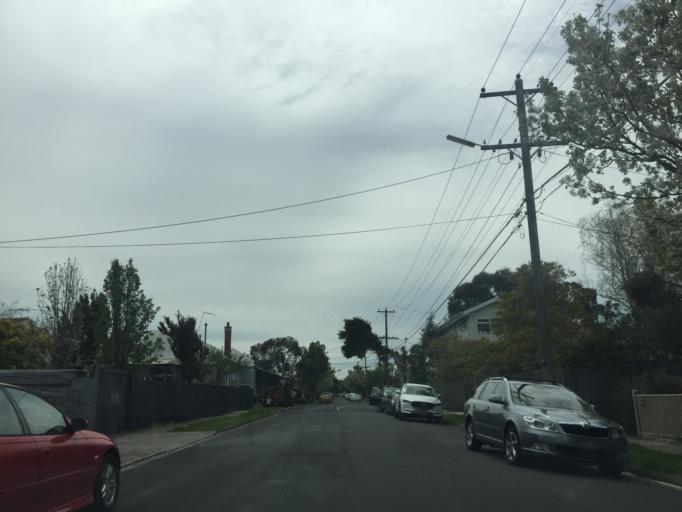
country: AU
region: Victoria
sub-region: Darebin
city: Northcote
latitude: -37.7752
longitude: 145.0034
